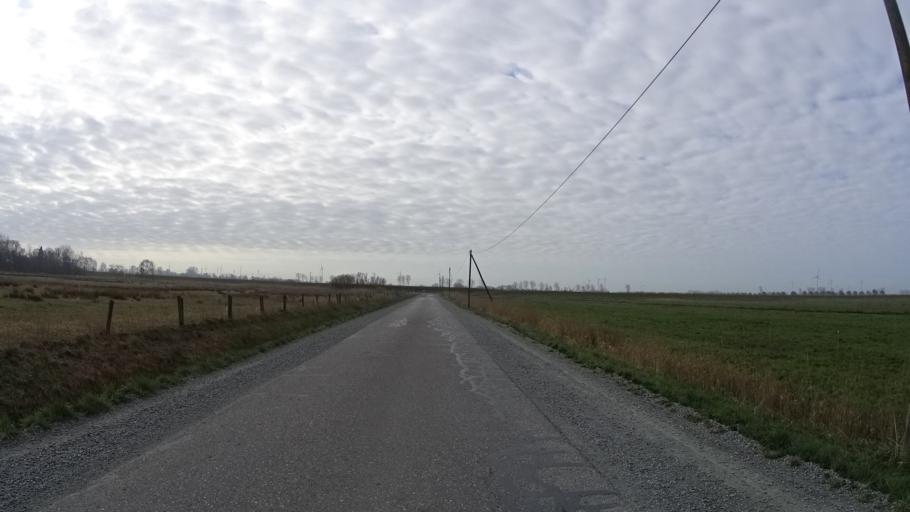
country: DE
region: Lower Saxony
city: Emden
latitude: 53.4044
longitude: 7.3190
